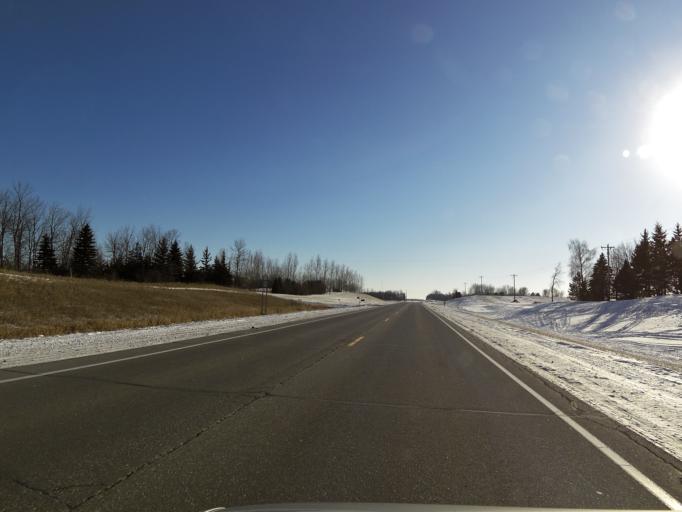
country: US
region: Minnesota
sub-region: Le Sueur County
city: New Prague
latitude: 44.5883
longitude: -93.5069
